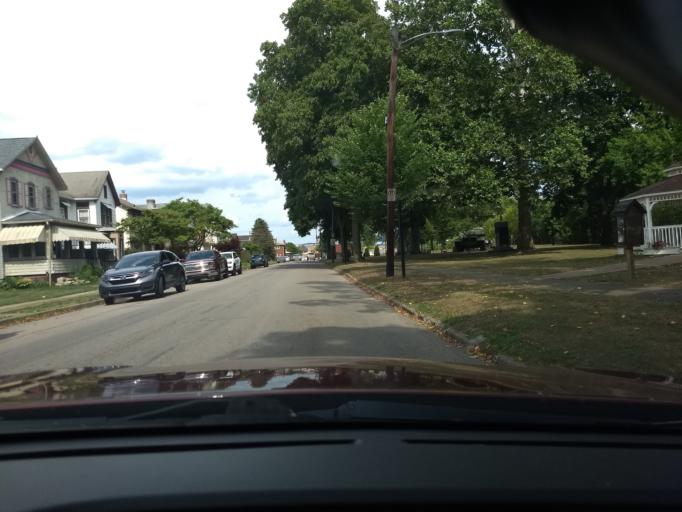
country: US
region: Pennsylvania
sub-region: Allegheny County
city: Brackenridge
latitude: 40.6012
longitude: -79.7491
